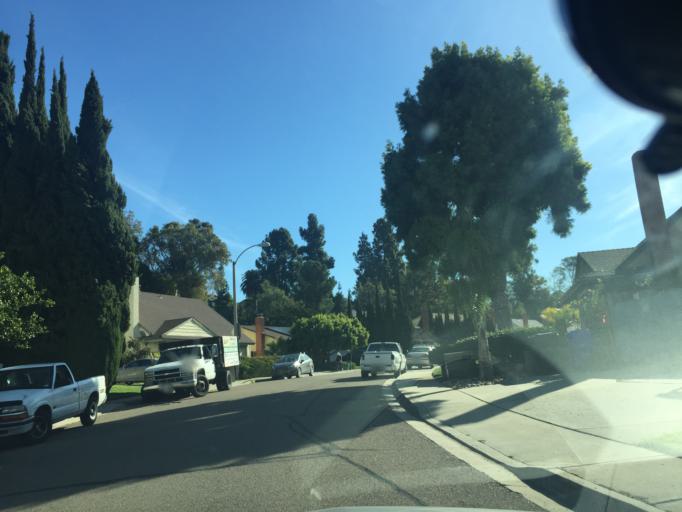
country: US
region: California
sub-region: San Diego County
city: Lemon Grove
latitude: 32.7653
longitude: -117.0792
